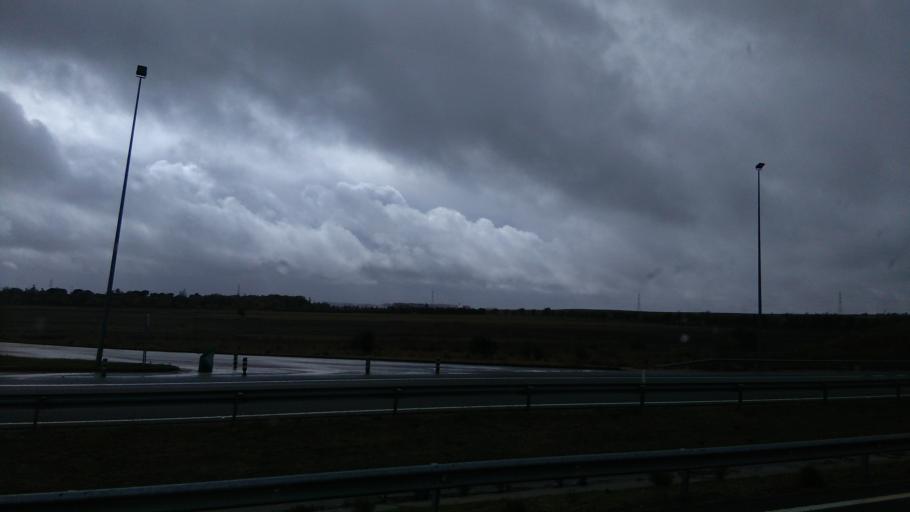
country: ES
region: Madrid
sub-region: Provincia de Madrid
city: Alcorcon
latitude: 40.3362
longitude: -3.8057
